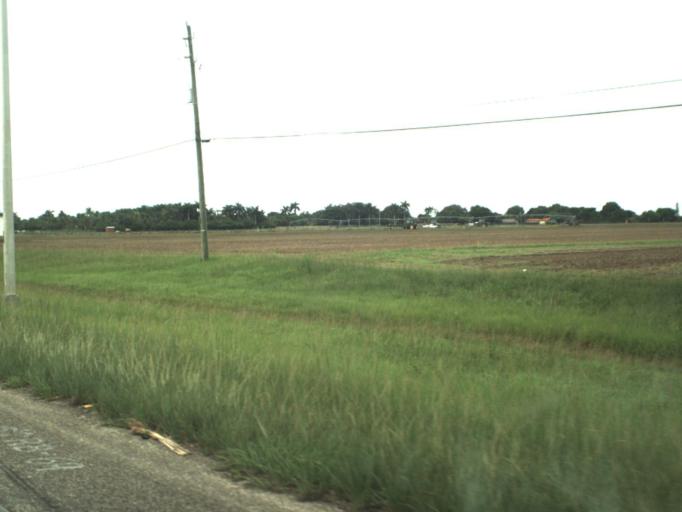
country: US
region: Florida
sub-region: Miami-Dade County
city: Richmond West
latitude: 25.6129
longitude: -80.4792
